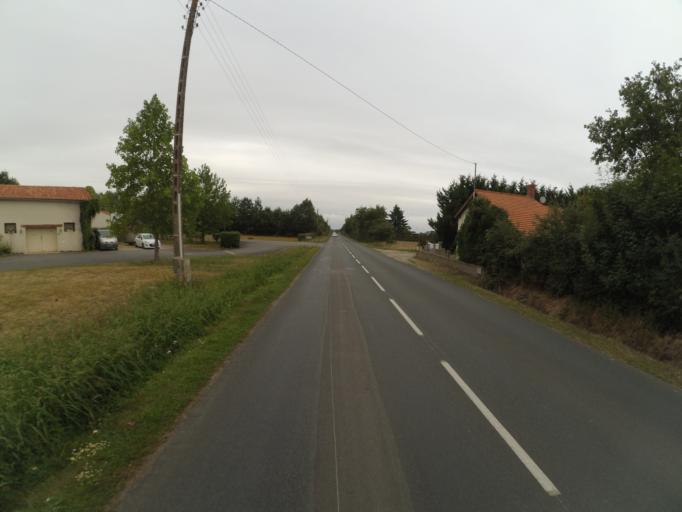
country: FR
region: Pays de la Loire
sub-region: Departement de la Vendee
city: Saint-Andre-Treize-Voies
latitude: 46.9186
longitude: -1.3891
